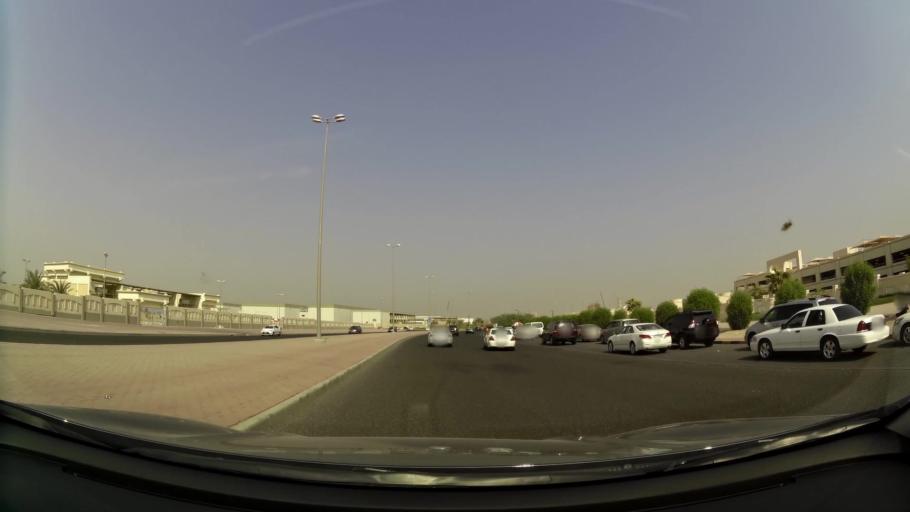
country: KW
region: Al Asimah
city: Ar Rabiyah
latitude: 29.2769
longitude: 47.9153
